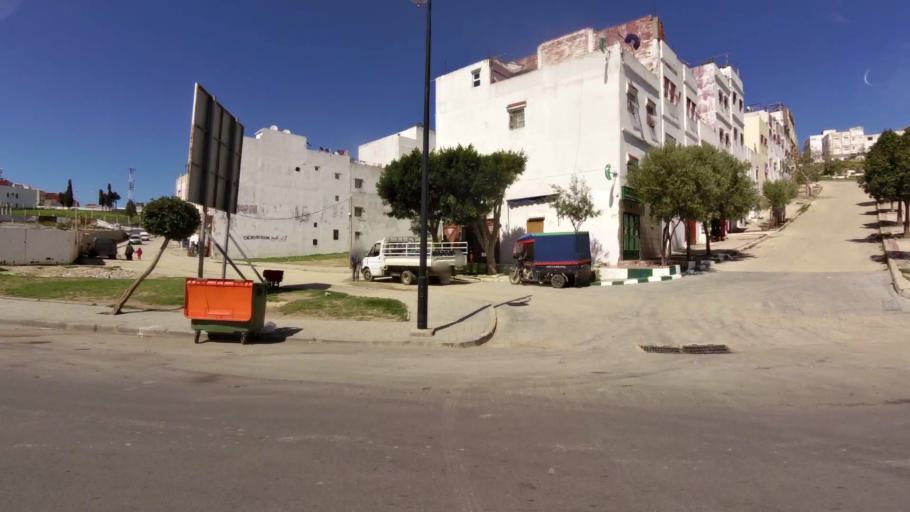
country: MA
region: Tanger-Tetouan
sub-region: Tanger-Assilah
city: Tangier
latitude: 35.7434
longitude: -5.8153
